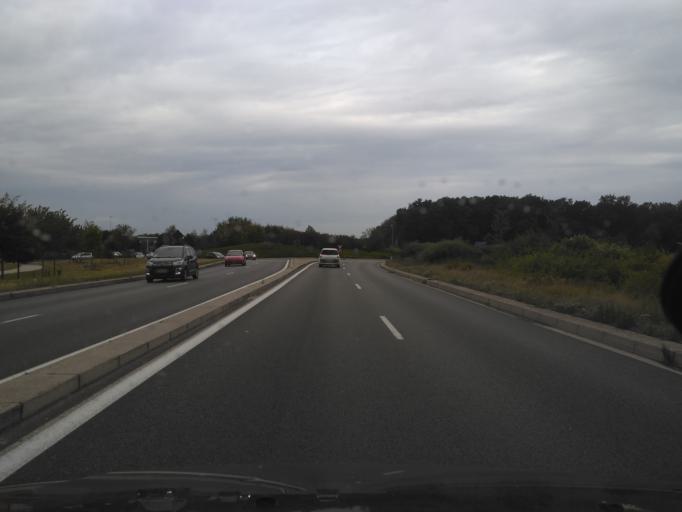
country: FR
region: Ile-de-France
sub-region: Departement de Seine-et-Marne
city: Savigny-le-Temple
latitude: 48.5886
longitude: 2.6024
